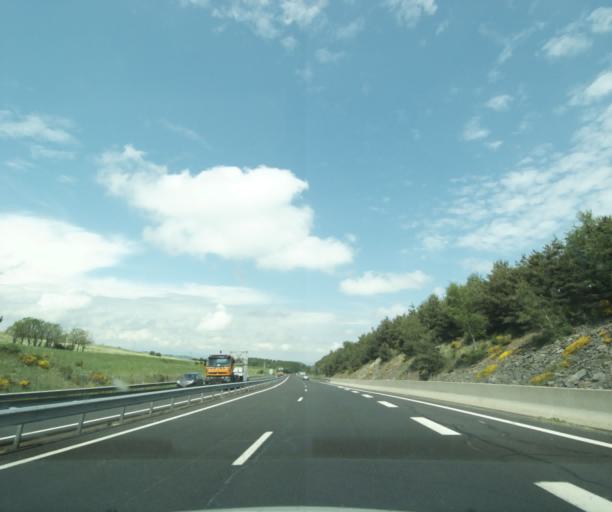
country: FR
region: Auvergne
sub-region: Departement du Cantal
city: Saint-Flour
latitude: 45.1164
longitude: 3.1406
